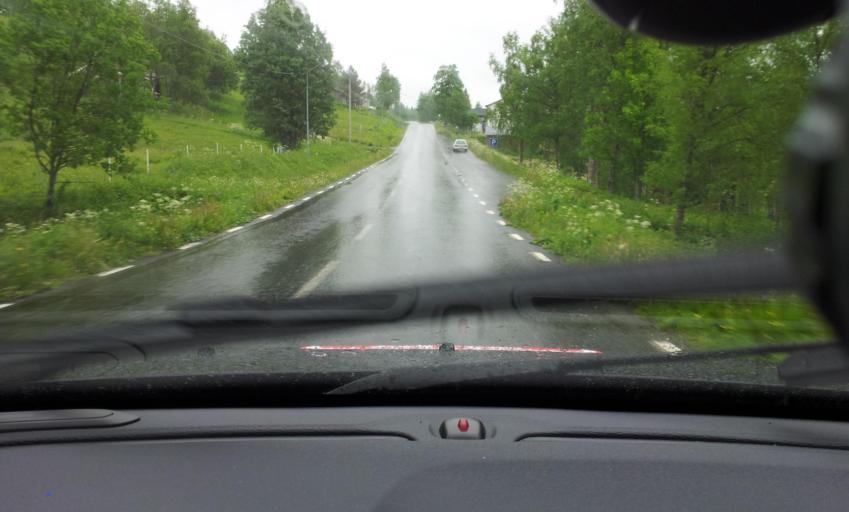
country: SE
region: Jaemtland
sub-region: Are Kommun
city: Are
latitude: 63.3149
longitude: 13.0749
